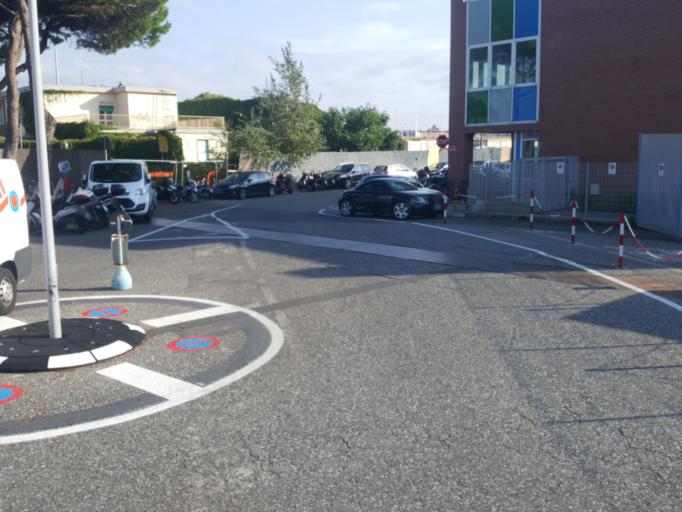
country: IT
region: Tuscany
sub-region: Provincia di Livorno
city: Livorno
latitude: 43.5447
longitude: 10.2990
